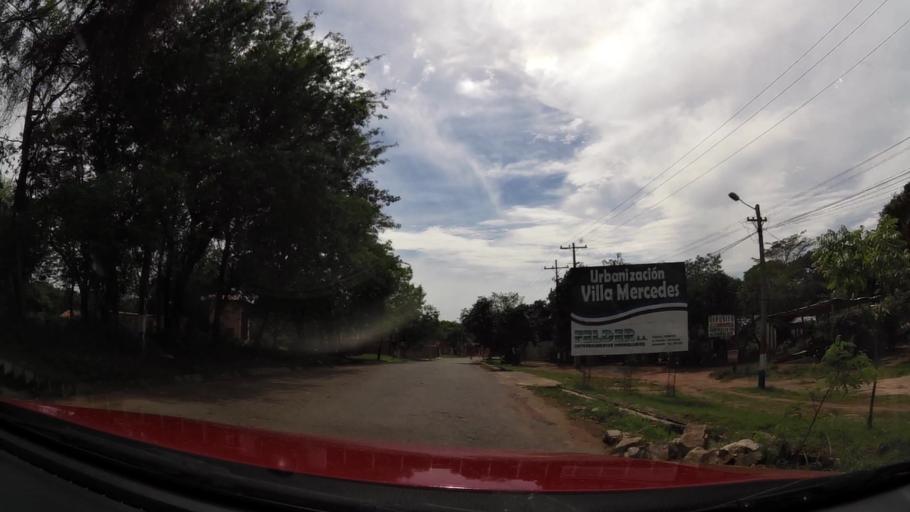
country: PY
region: Central
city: Limpio
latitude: -25.1817
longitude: -57.4499
